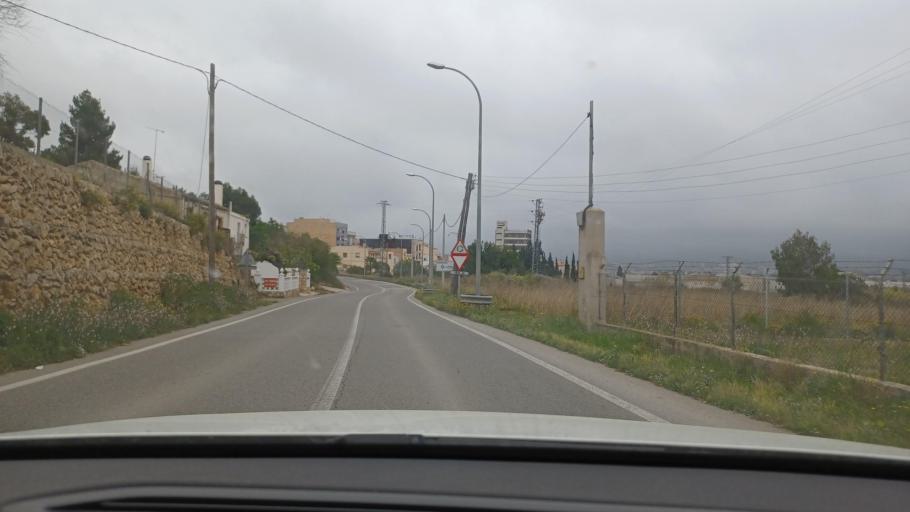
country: ES
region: Catalonia
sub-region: Provincia de Tarragona
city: Tortosa
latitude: 40.8066
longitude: 0.4906
